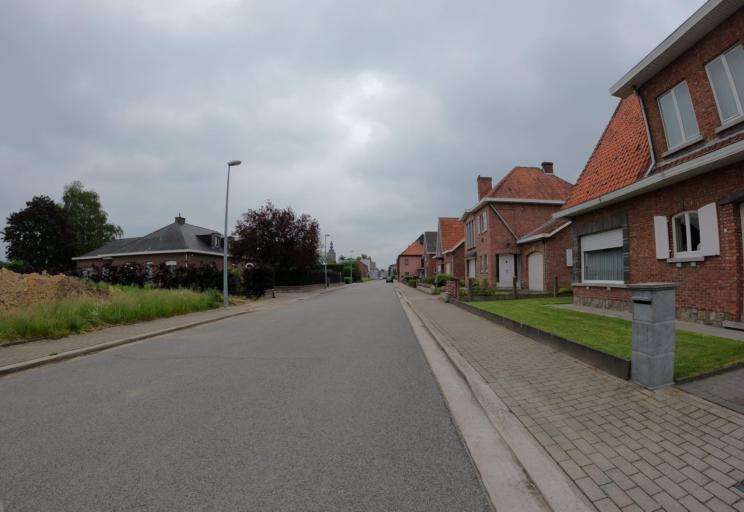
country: BE
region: Flanders
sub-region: Provincie Oost-Vlaanderen
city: Dendermonde
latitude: 51.0568
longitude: 4.1045
